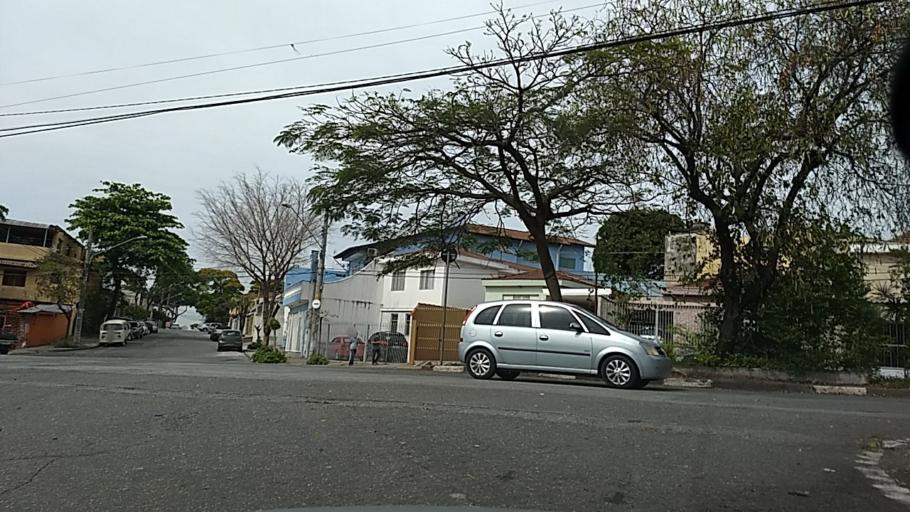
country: BR
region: Sao Paulo
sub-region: Guarulhos
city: Guarulhos
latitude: -23.5030
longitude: -46.5700
